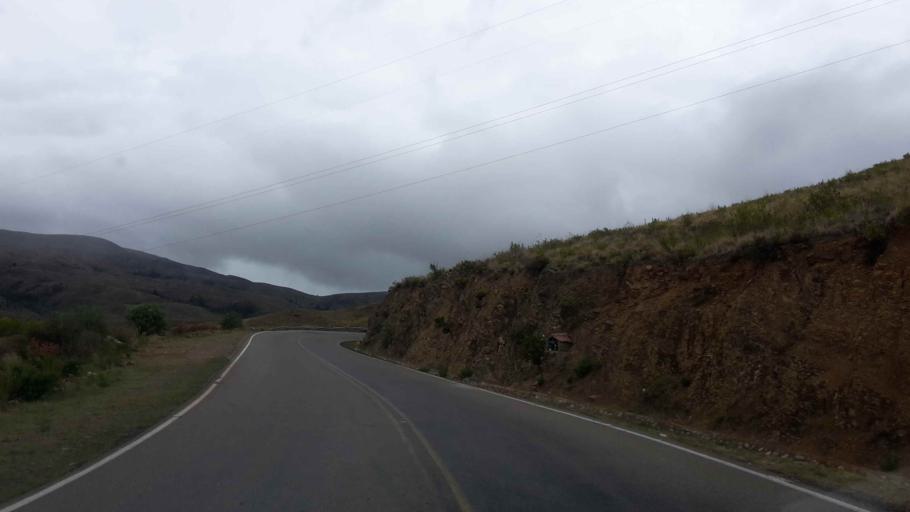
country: BO
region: Cochabamba
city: Punata
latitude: -17.4861
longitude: -65.7797
